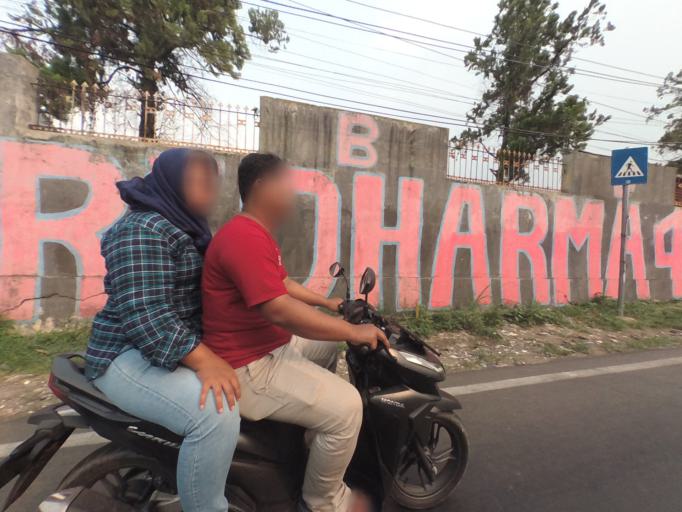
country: ID
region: West Java
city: Ciampea
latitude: -6.5730
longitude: 106.6664
